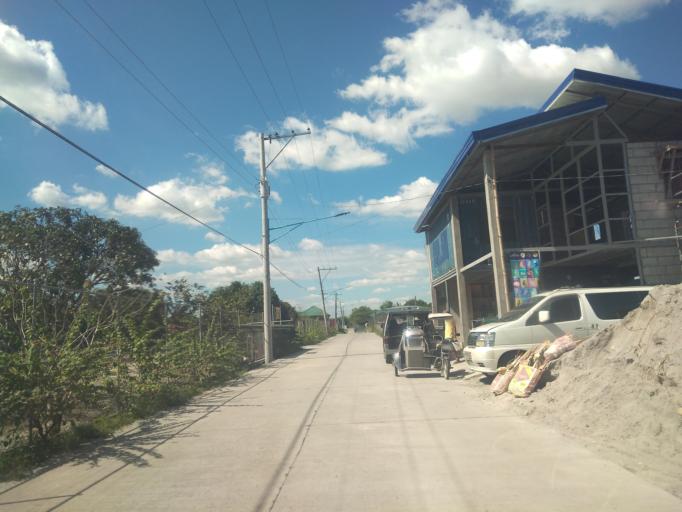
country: PH
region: Central Luzon
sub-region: Province of Pampanga
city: Bacolor
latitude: 15.0075
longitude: 120.6466
